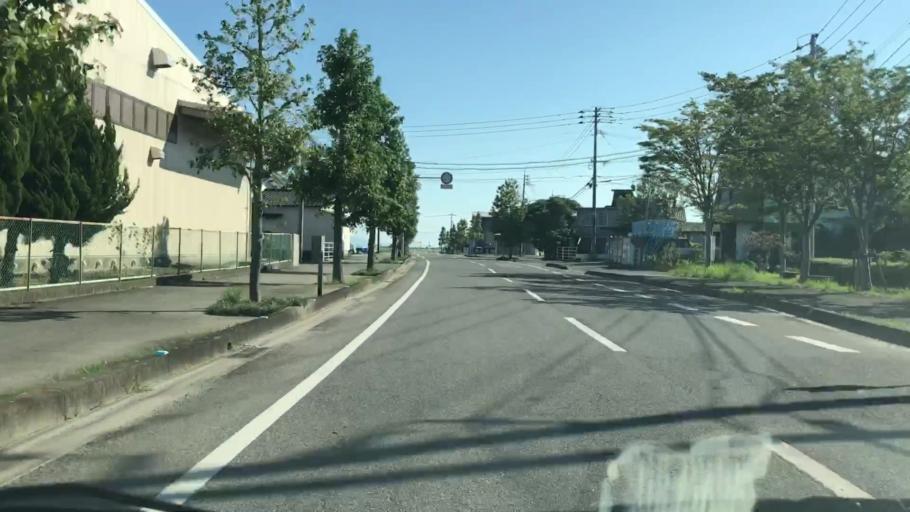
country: JP
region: Saga Prefecture
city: Okawa
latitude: 33.1812
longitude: 130.3134
